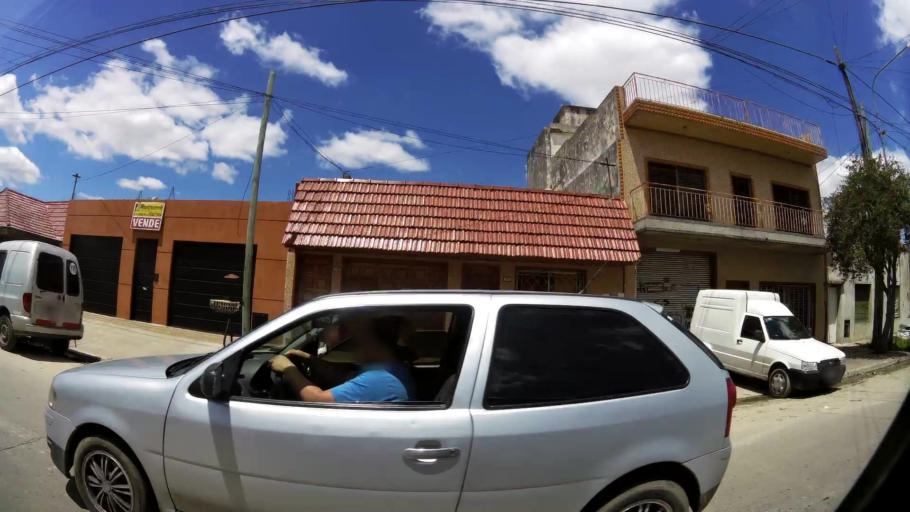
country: AR
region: Buenos Aires
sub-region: Partido de Lanus
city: Lanus
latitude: -34.7056
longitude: -58.4210
